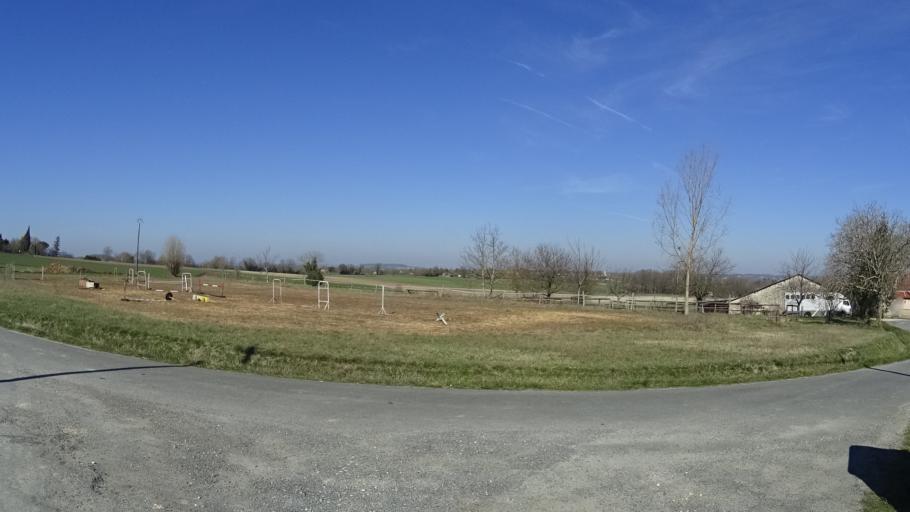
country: FR
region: Aquitaine
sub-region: Departement de la Dordogne
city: Riberac
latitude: 45.2217
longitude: 0.3310
